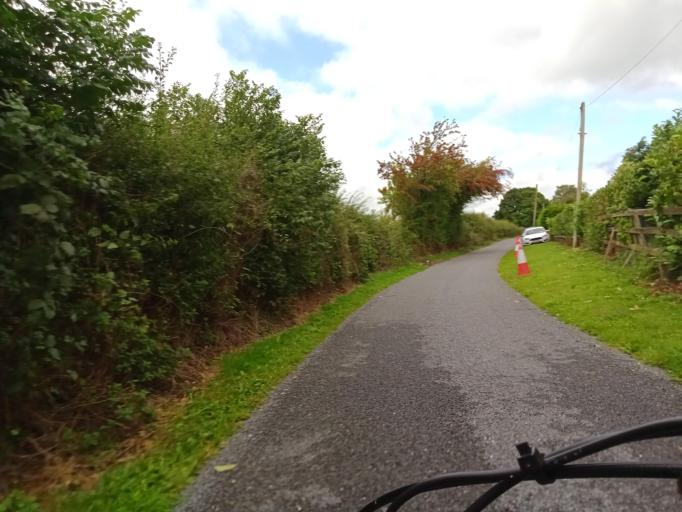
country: IE
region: Leinster
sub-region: Kilkenny
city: Callan
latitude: 52.5302
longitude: -7.2873
